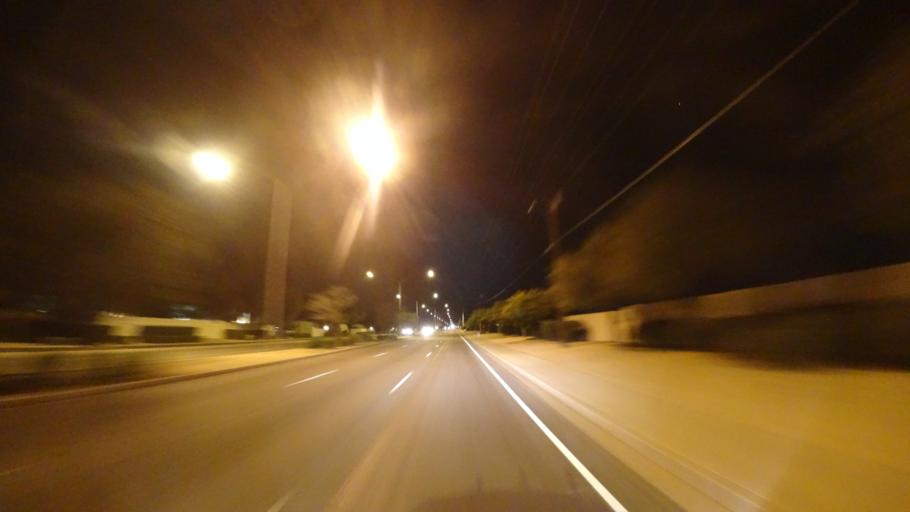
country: US
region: Arizona
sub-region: Maricopa County
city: Gilbert
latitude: 33.4065
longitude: -111.6847
